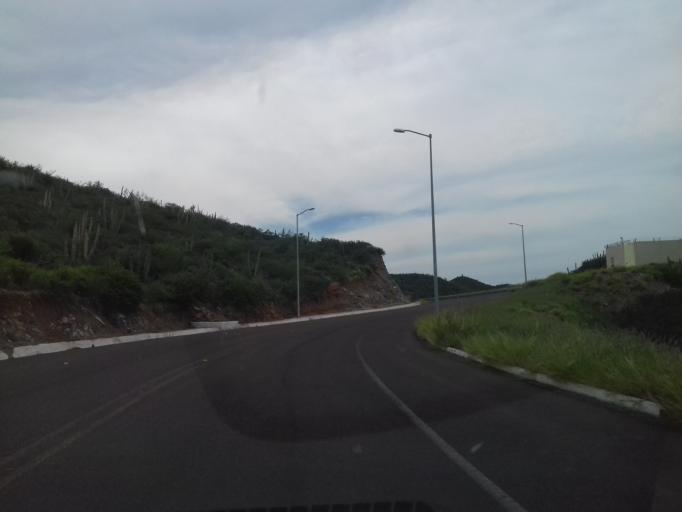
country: MX
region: Sonora
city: Heroica Guaymas
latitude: 27.9402
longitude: -111.0962
